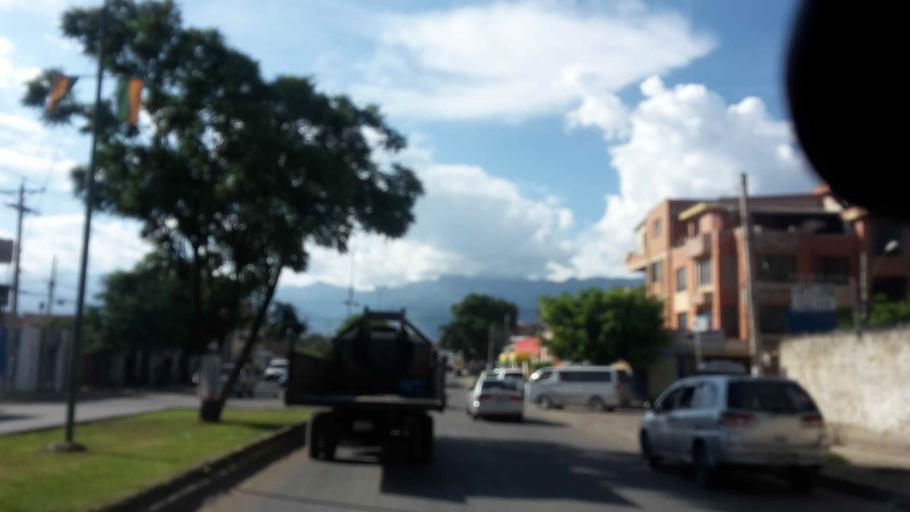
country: BO
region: Cochabamba
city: Cochabamba
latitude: -17.4088
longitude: -66.1751
